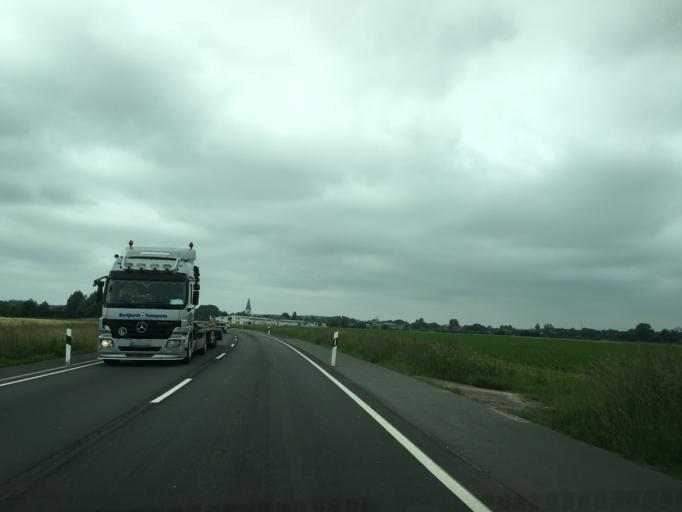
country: DE
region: North Rhine-Westphalia
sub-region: Regierungsbezirk Munster
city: Laer
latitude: 52.0547
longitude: 7.3784
